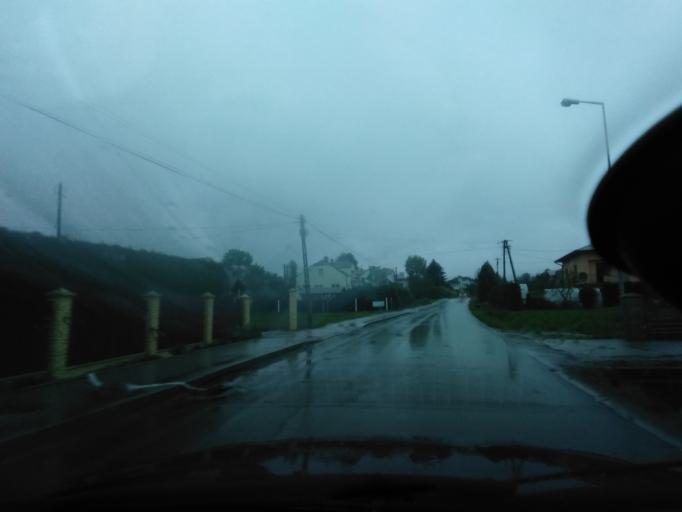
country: PL
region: Subcarpathian Voivodeship
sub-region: Powiat krosnienski
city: Korczyna
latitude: 49.7075
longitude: 21.8121
